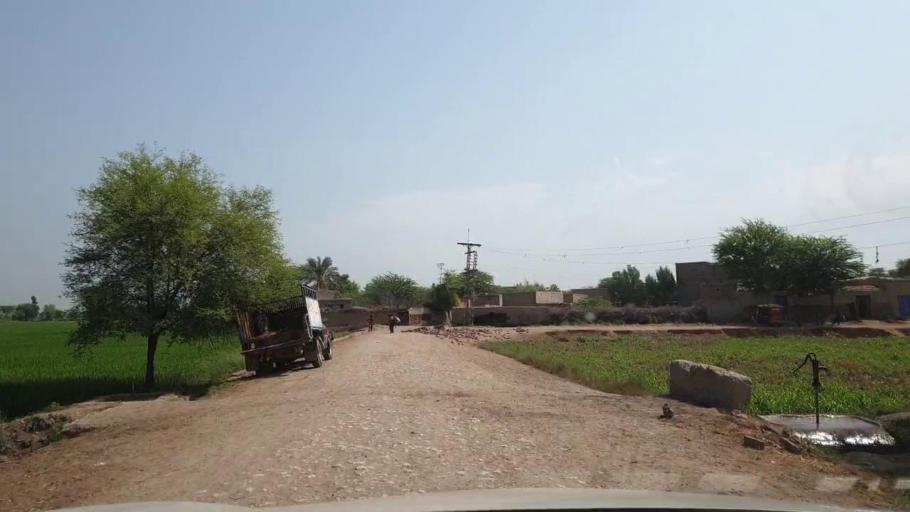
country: PK
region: Sindh
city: Ratodero
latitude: 27.8204
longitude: 68.2914
